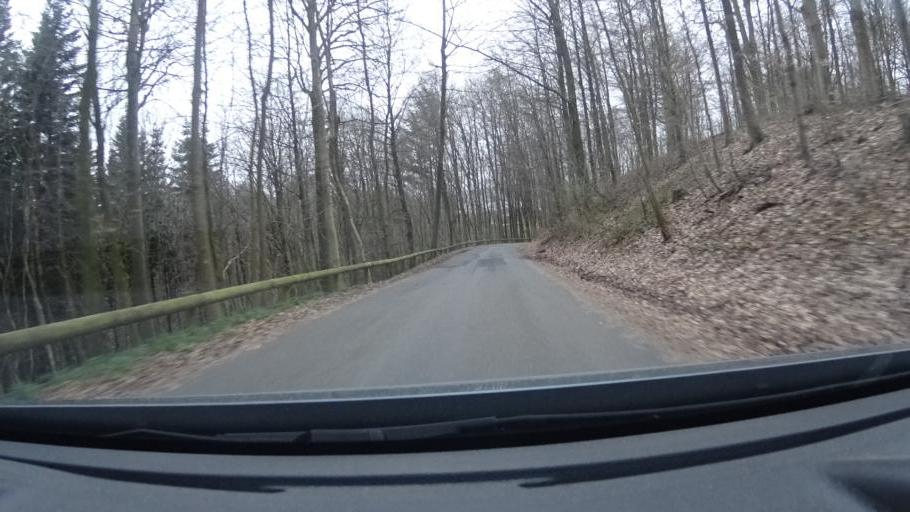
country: DK
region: South Denmark
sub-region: Vejle Kommune
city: Vejle
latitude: 55.7098
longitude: 9.5808
